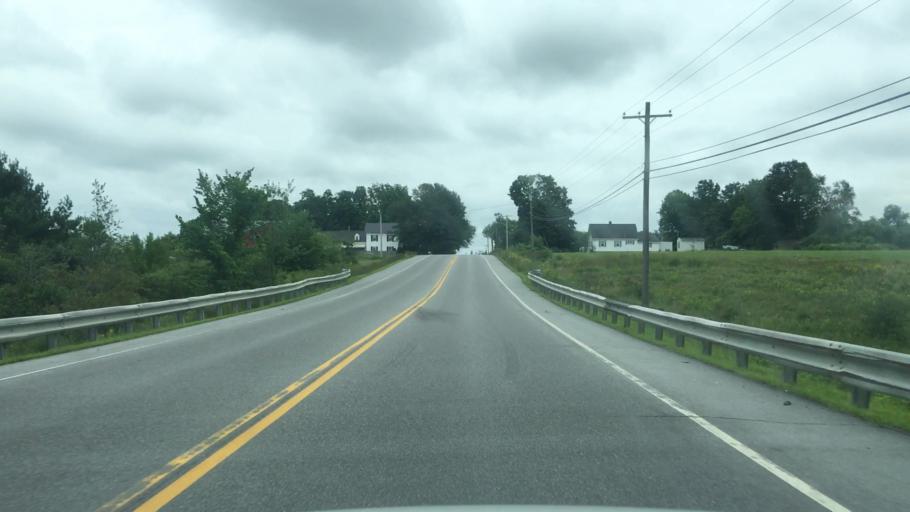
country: US
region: Maine
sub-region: York County
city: Biddeford
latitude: 43.5230
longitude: -70.4895
